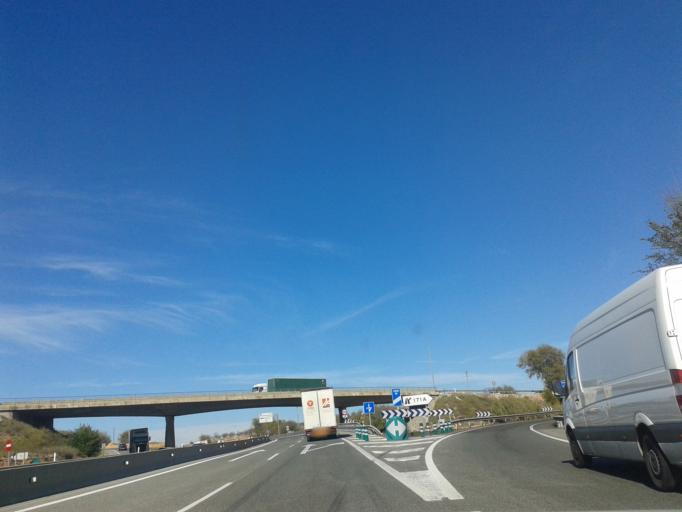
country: ES
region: Castille-La Mancha
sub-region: Provincia de Albacete
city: Caudete
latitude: 38.7303
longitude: -0.9393
